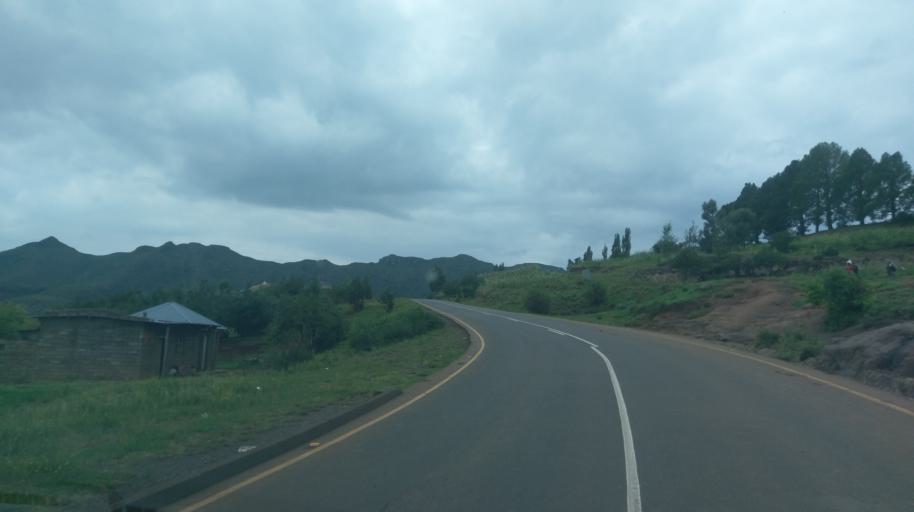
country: LS
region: Butha-Buthe
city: Butha-Buthe
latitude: -29.0355
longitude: 28.2839
